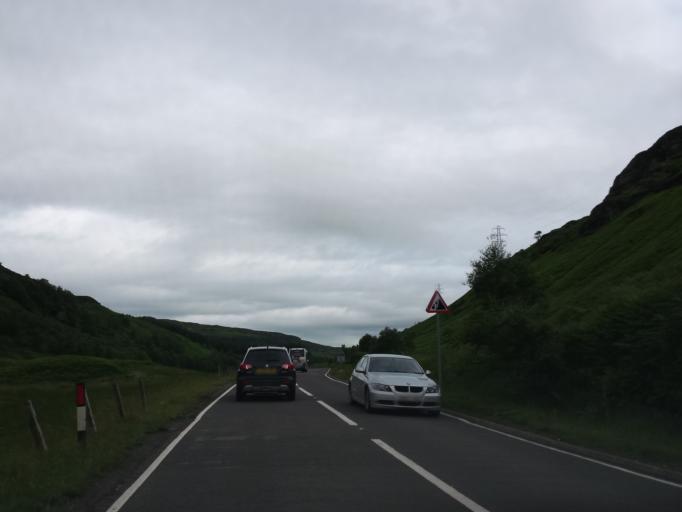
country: GB
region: Scotland
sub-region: Stirling
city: Callander
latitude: 56.4116
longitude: -4.3188
